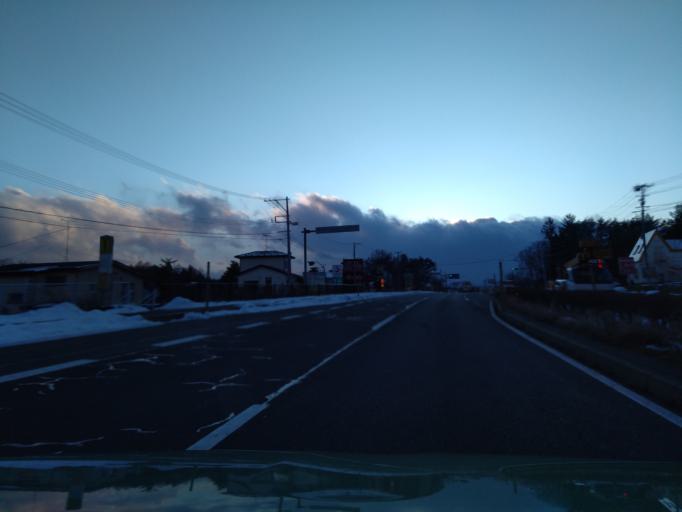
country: JP
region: Iwate
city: Shizukuishi
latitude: 39.7000
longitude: 141.0272
